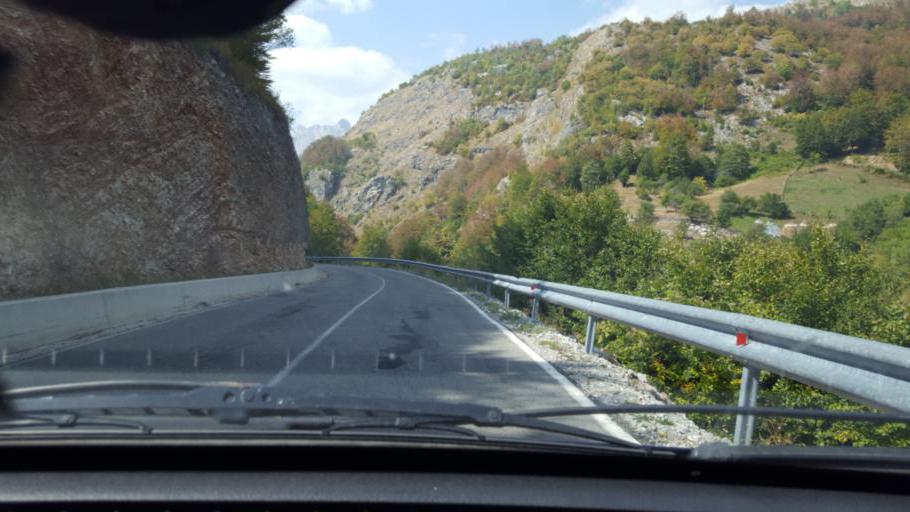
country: AL
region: Kukes
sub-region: Rrethi i Tropojes
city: Valbone
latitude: 42.5367
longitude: 19.6881
